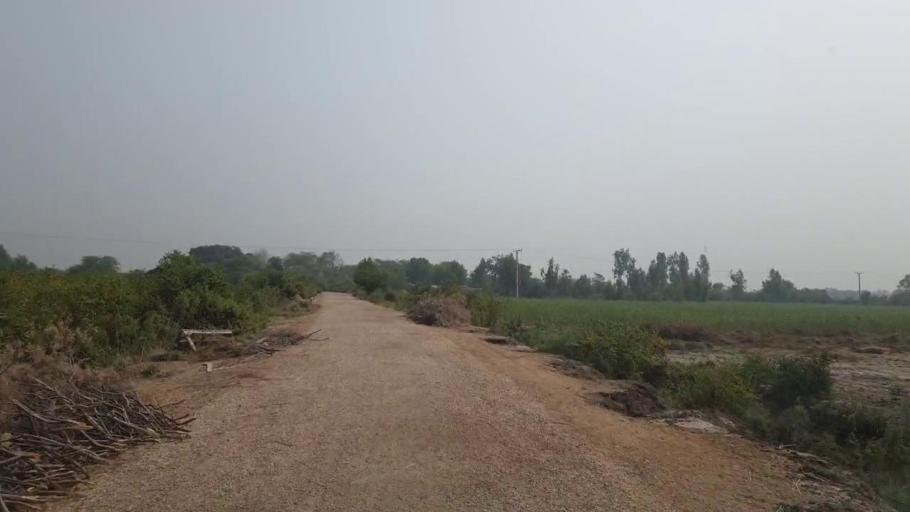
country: PK
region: Sindh
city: Kario
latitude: 24.6571
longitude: 68.6590
